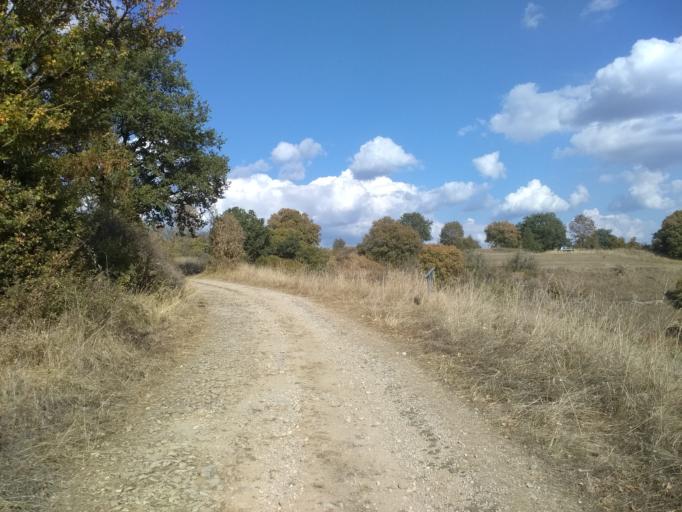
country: FR
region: Midi-Pyrenees
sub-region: Departement de l'Aveyron
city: Bozouls
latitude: 44.4767
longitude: 2.6908
